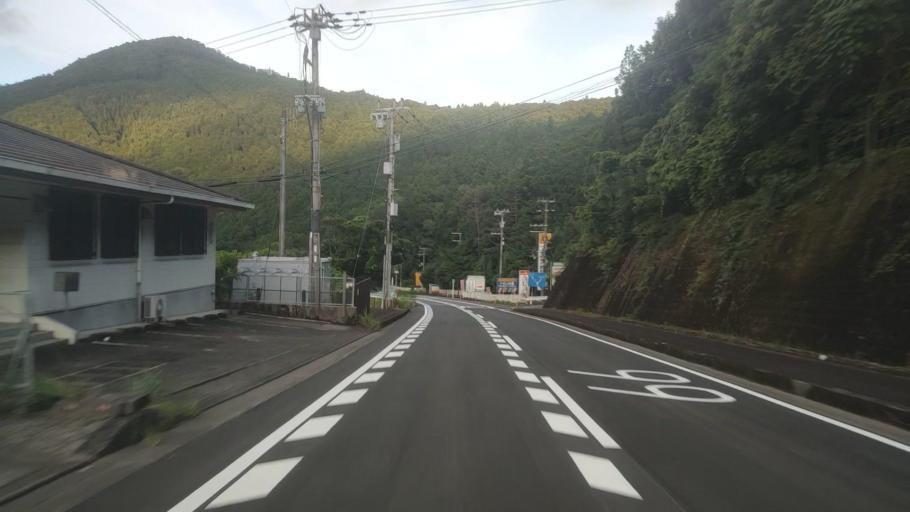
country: JP
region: Wakayama
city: Shingu
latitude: 33.8177
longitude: 135.7628
